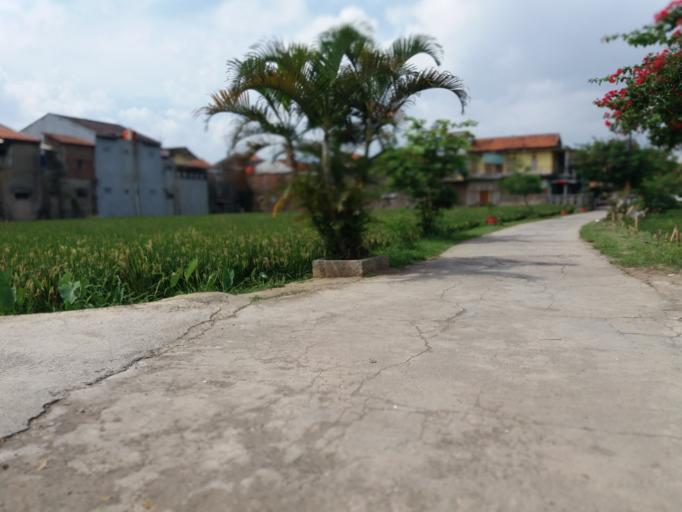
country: ID
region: West Java
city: Bandung
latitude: -6.9192
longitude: 107.6516
